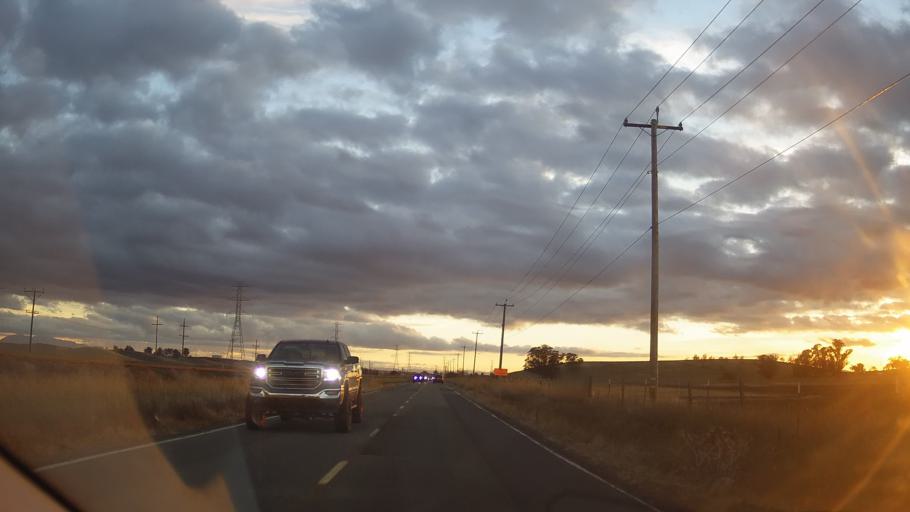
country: US
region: California
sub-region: Solano County
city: Vacaville
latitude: 38.3079
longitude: -121.9457
